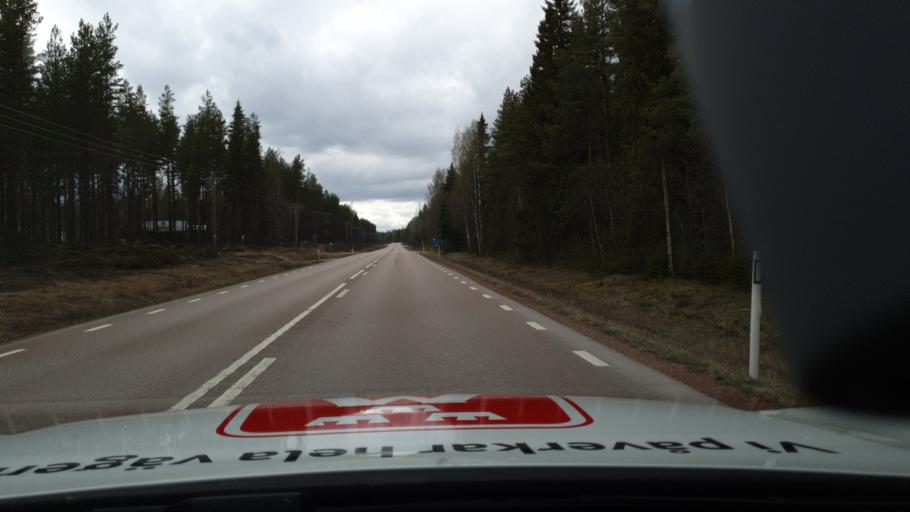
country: SE
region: Jaemtland
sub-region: Ragunda Kommun
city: Hammarstrand
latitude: 63.1728
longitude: 15.8775
